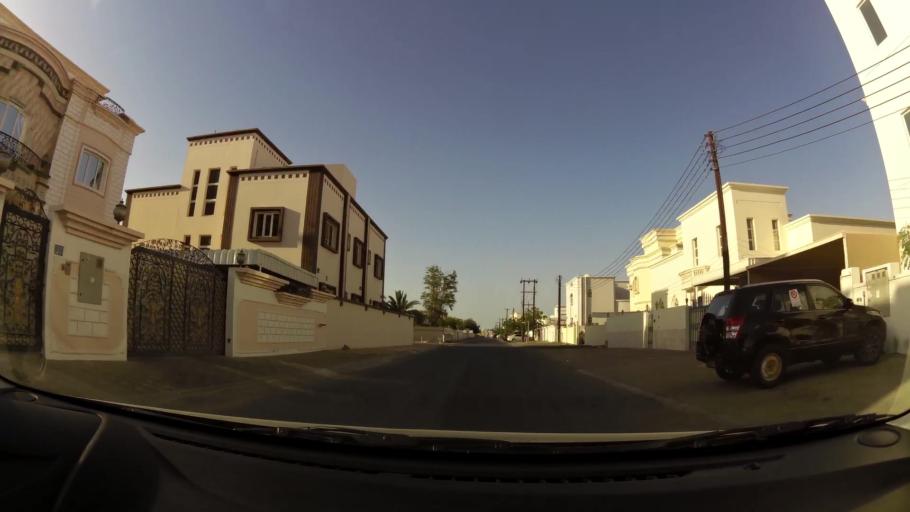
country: OM
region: Muhafazat Masqat
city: As Sib al Jadidah
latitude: 23.6329
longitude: 58.1923
